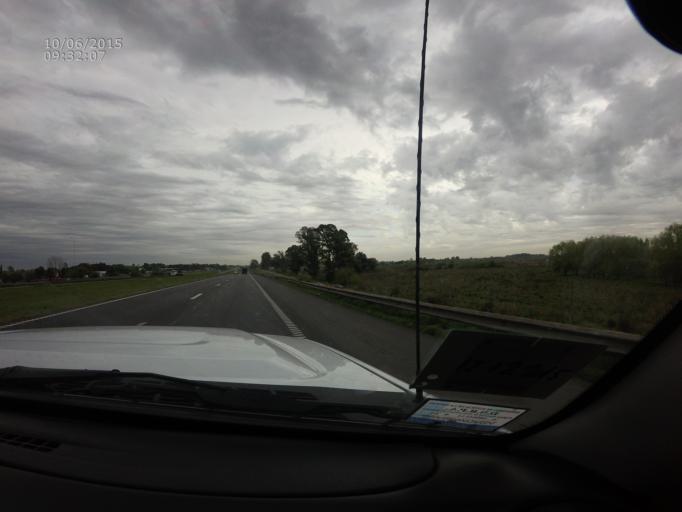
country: AR
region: Buenos Aires
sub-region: Partido de Zarate
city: Zarate
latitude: -34.1295
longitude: -59.0734
